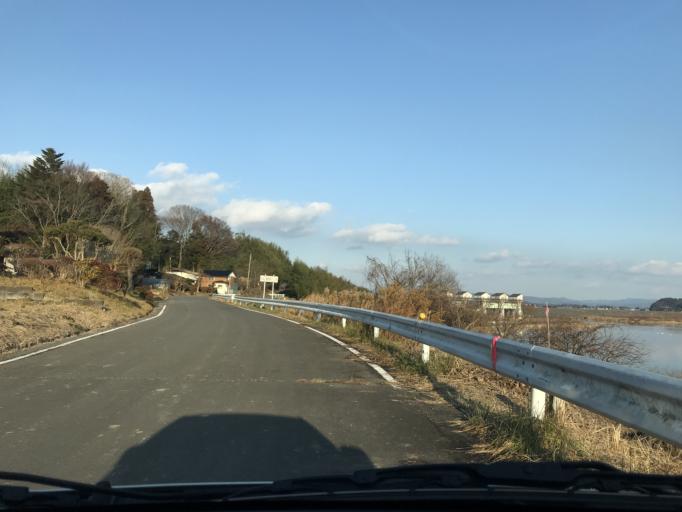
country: JP
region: Miyagi
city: Wakuya
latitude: 38.7086
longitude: 141.1405
